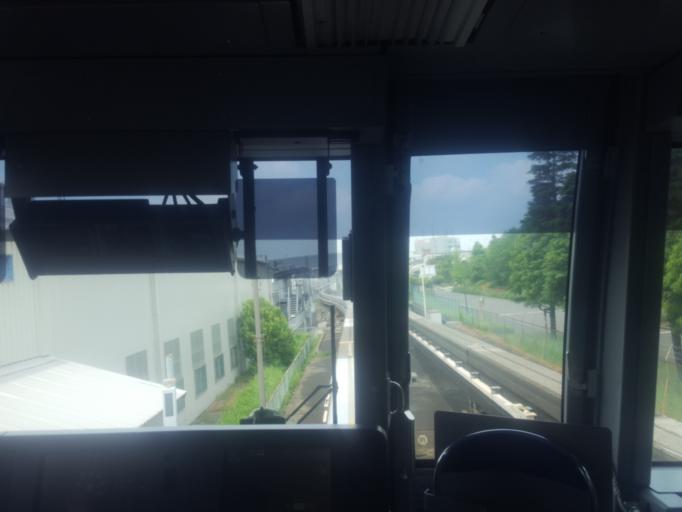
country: JP
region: Kanagawa
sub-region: Kawasaki-shi
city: Kawasaki
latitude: 35.5690
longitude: 139.7495
